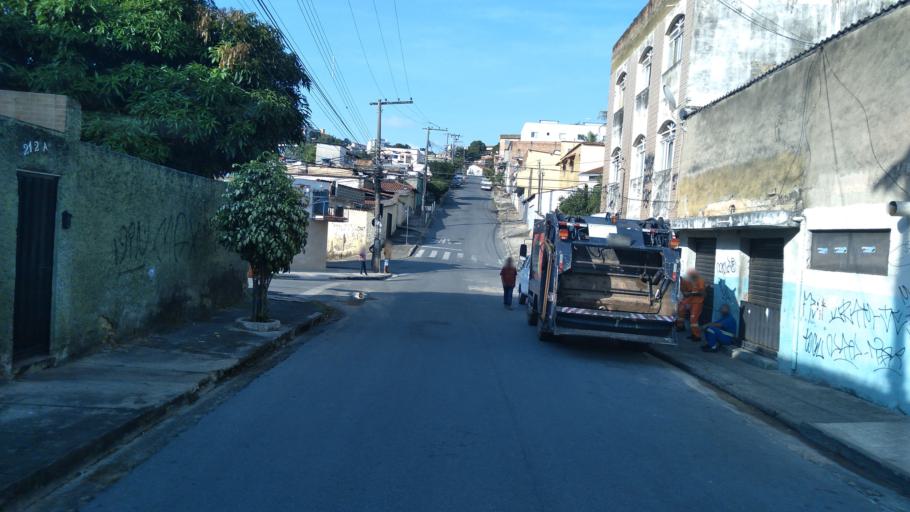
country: BR
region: Minas Gerais
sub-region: Belo Horizonte
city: Belo Horizonte
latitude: -19.8982
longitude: -43.9391
